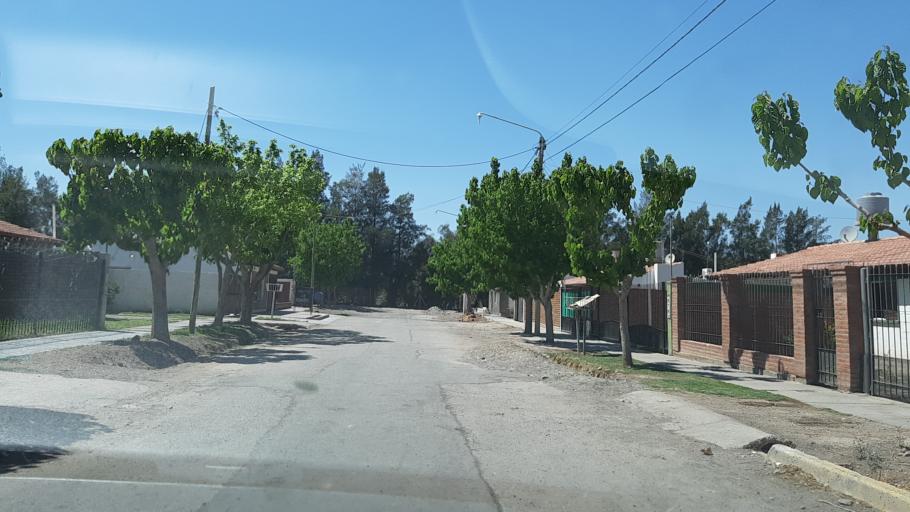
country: AR
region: San Juan
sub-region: Departamento de Zonda
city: Zonda
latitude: -31.5388
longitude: -68.7510
